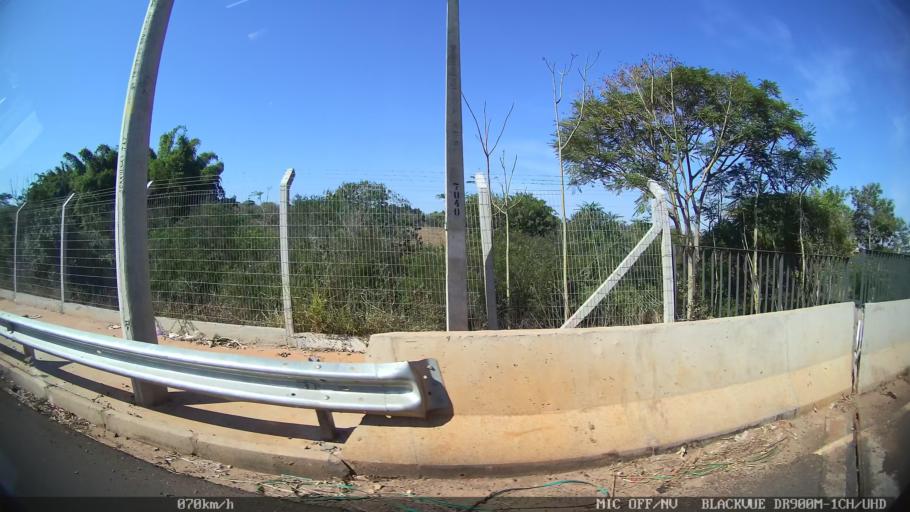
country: BR
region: Sao Paulo
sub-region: Sao Jose Do Rio Preto
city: Sao Jose do Rio Preto
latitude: -20.7631
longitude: -49.3760
